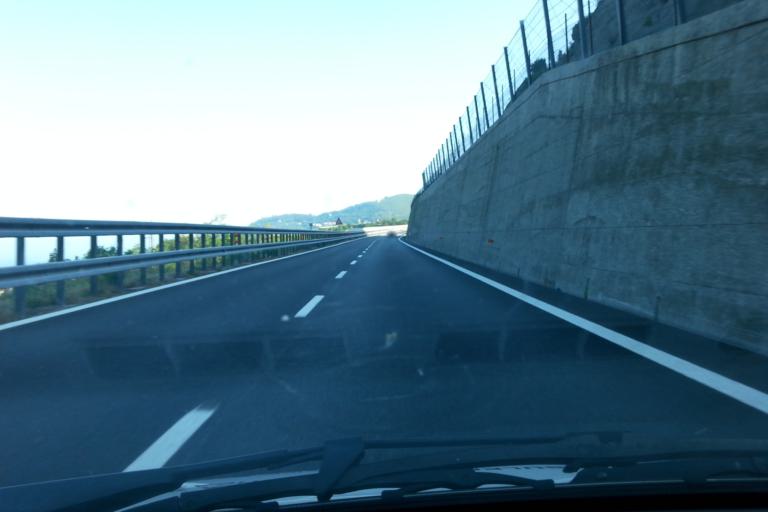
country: IT
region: Liguria
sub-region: Provincia di Savona
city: Spotorno
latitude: 44.2356
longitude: 8.3990
